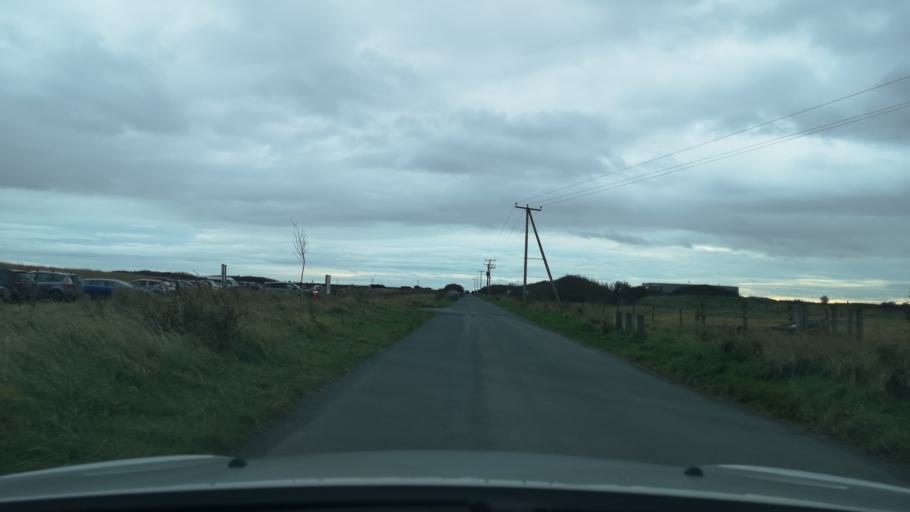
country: GB
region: England
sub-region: East Riding of Yorkshire
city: Easington
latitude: 53.6175
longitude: 0.1400
